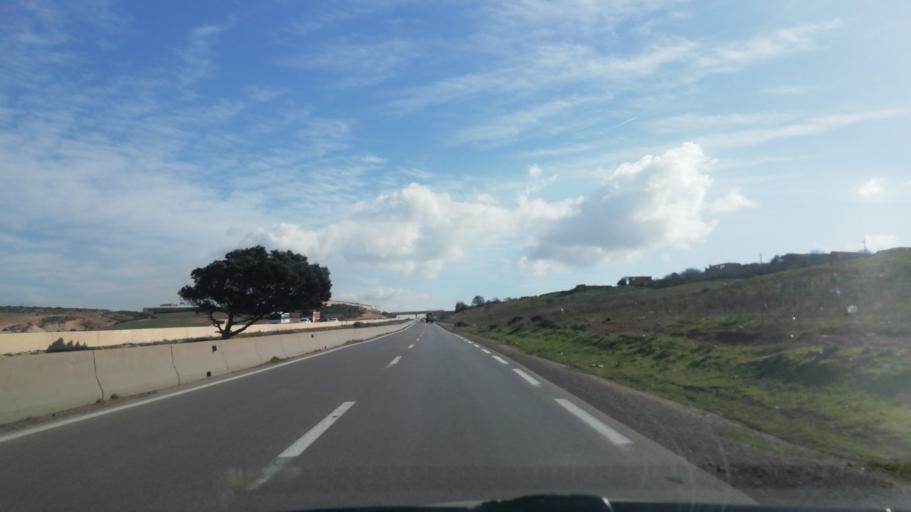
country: DZ
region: Oran
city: Ain el Bya
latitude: 35.7676
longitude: -0.2283
